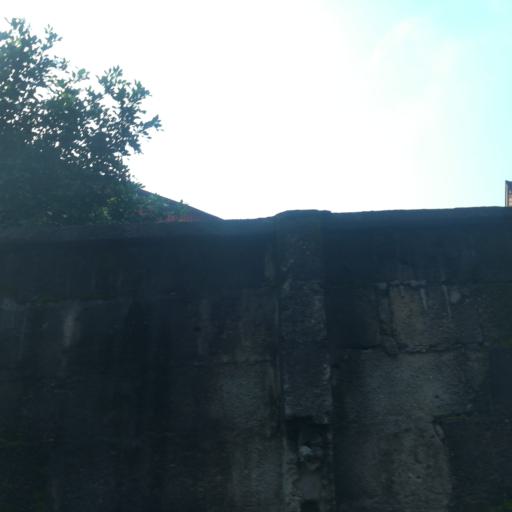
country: NG
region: Rivers
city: Port Harcourt
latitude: 4.8609
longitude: 6.9657
